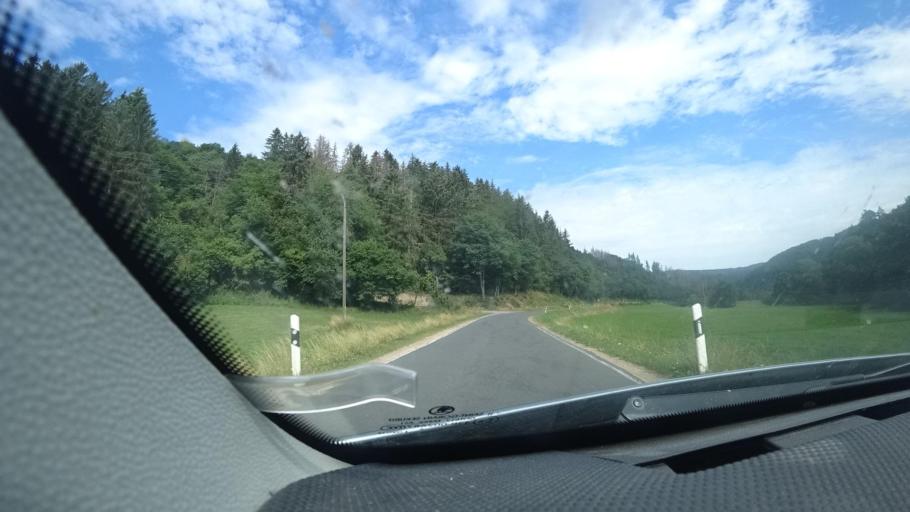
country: DE
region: Rheinland-Pfalz
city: Heckenbach
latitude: 50.4721
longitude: 7.0611
